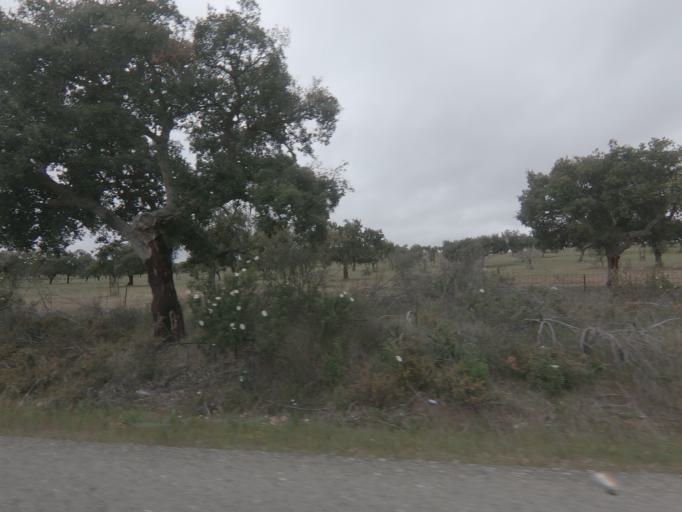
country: ES
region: Extremadura
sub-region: Provincia de Badajoz
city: Puebla de Obando
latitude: 39.2175
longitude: -6.5800
